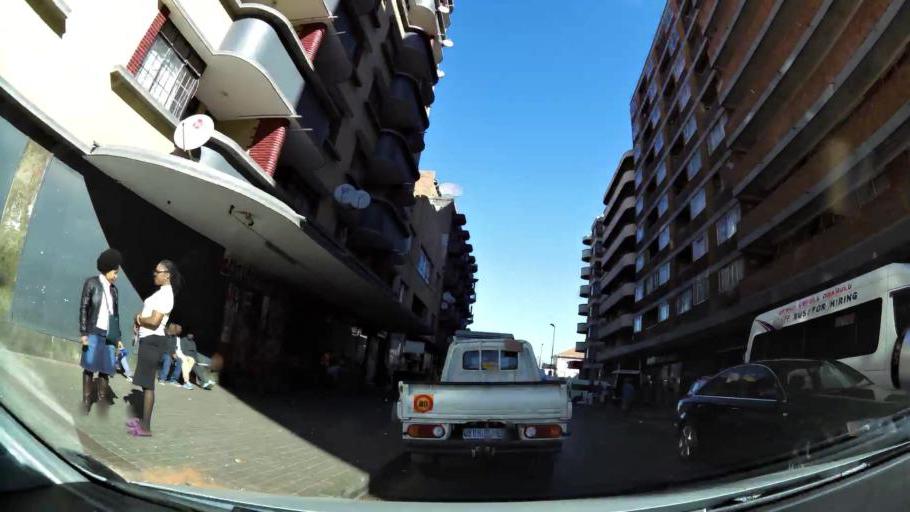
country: ZA
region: Gauteng
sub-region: City of Johannesburg Metropolitan Municipality
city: Johannesburg
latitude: -26.1962
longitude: 28.0456
